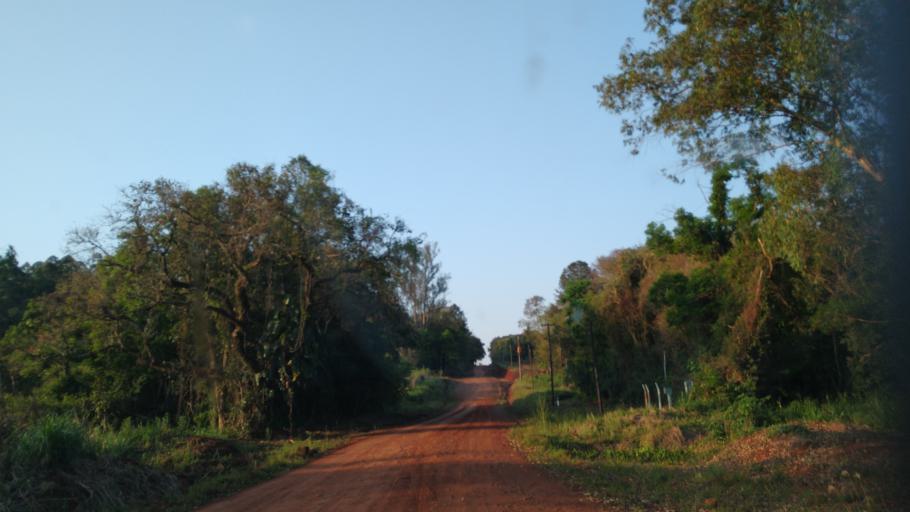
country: AR
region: Misiones
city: Jardin America
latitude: -27.0749
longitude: -55.2703
